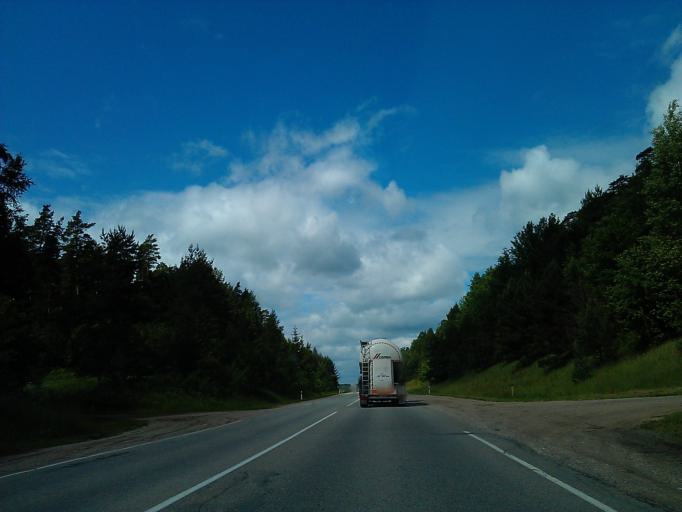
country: LV
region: Tukuma Rajons
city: Tukums
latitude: 56.9458
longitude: 23.1405
